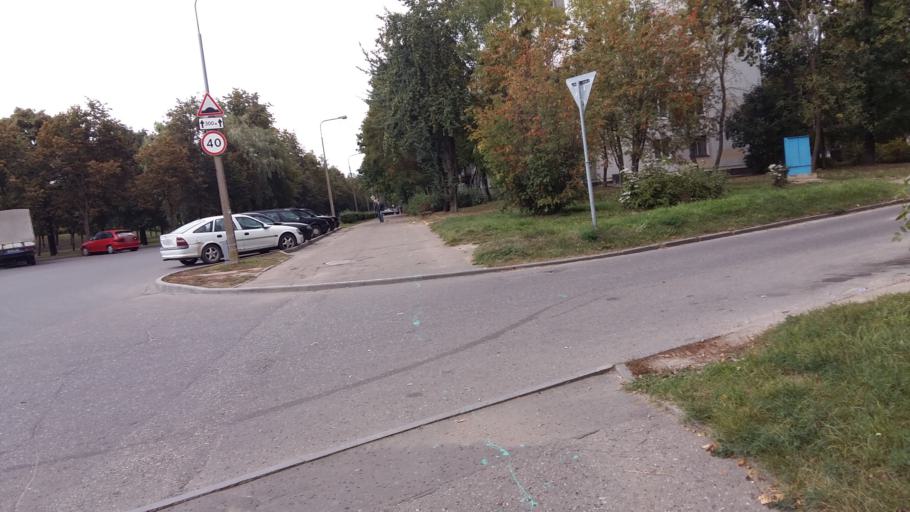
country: BY
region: Grodnenskaya
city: Hrodna
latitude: 53.7031
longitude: 23.7970
